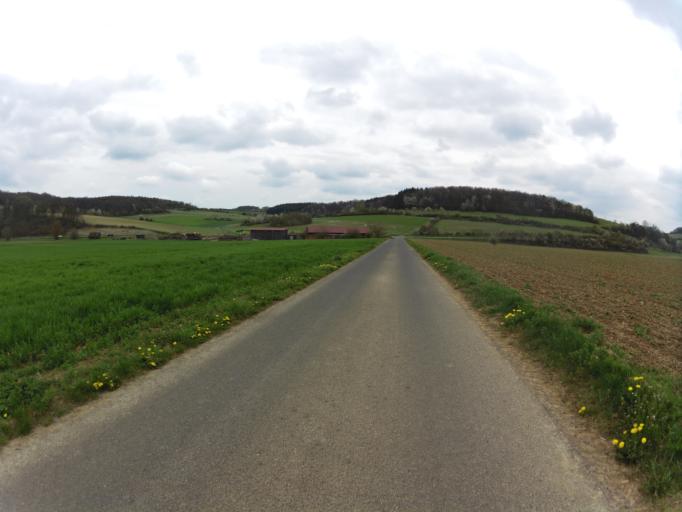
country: DE
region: Bavaria
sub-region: Regierungsbezirk Unterfranken
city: Greussenheim
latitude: 49.8194
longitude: 9.7713
